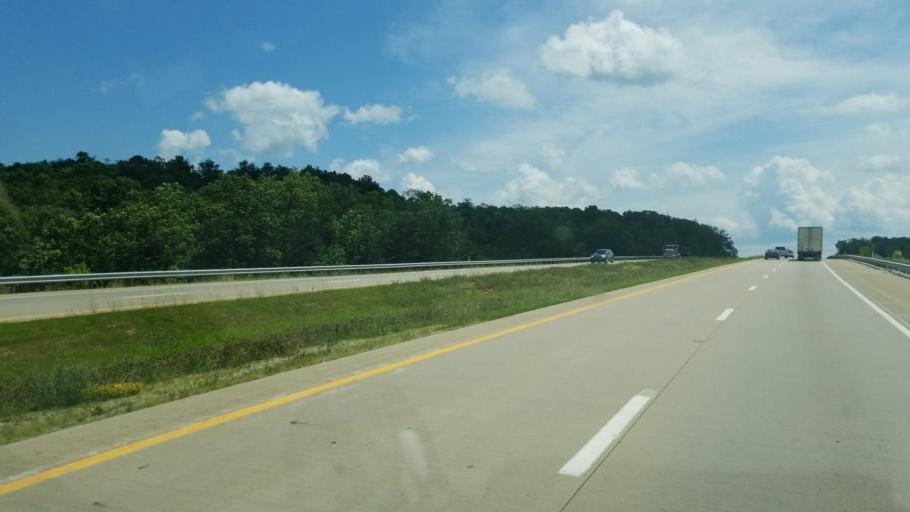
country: US
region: West Virginia
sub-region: Mason County
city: Point Pleasant
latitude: 38.7766
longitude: -82.0602
